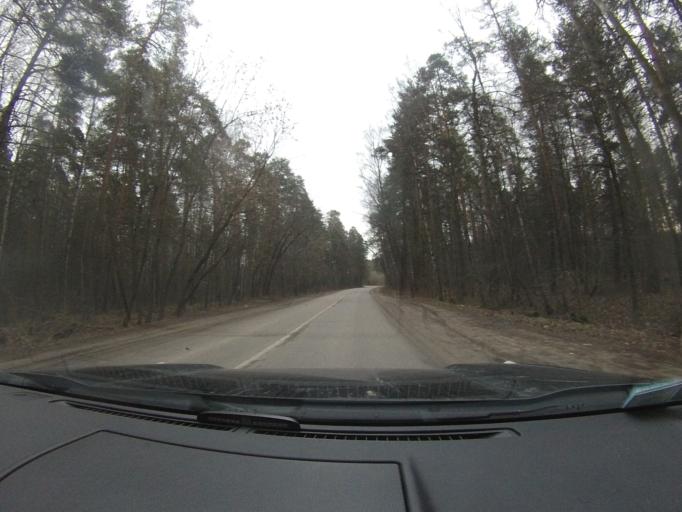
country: RU
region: Moskovskaya
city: Voskresensk
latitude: 55.3362
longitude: 38.6748
